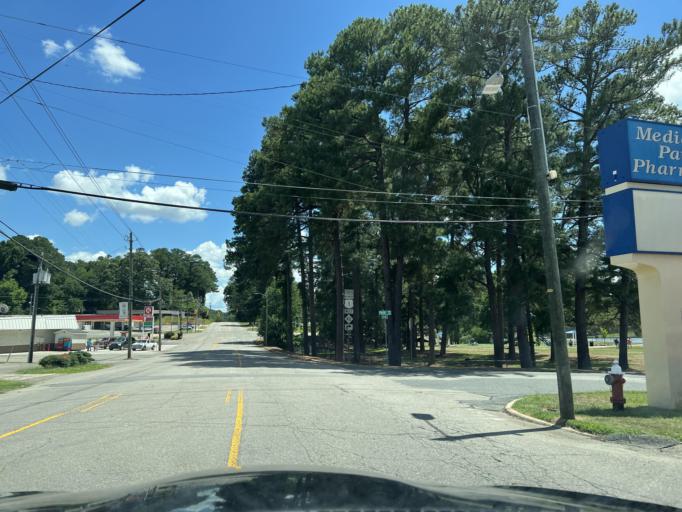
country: US
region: North Carolina
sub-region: Lee County
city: Sanford
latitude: 35.4755
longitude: -79.1875
